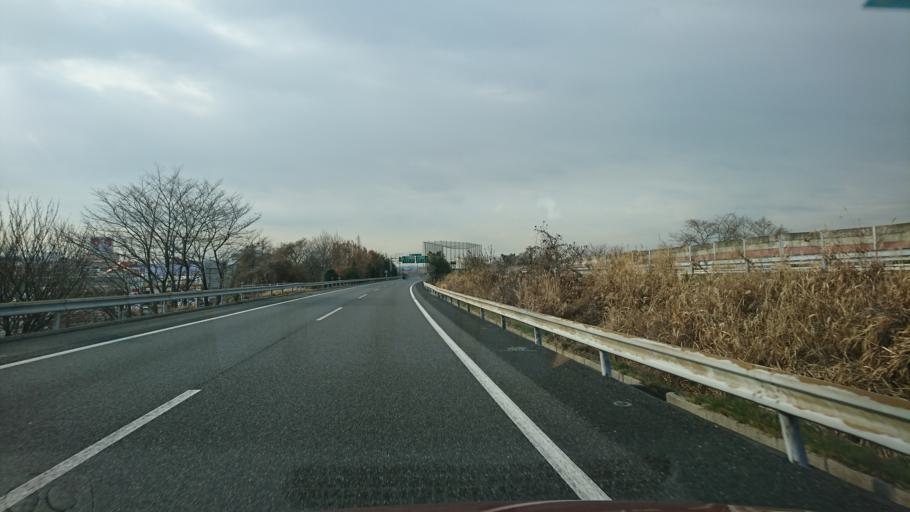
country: JP
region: Okayama
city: Kurashiki
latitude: 34.6323
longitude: 133.8032
